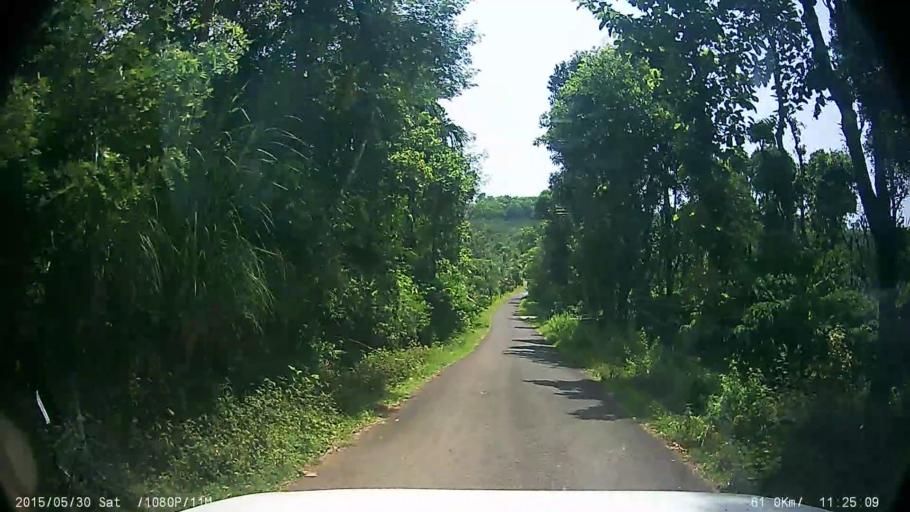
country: IN
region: Kerala
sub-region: Wayanad
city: Panamaram
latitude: 11.8086
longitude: 76.0313
